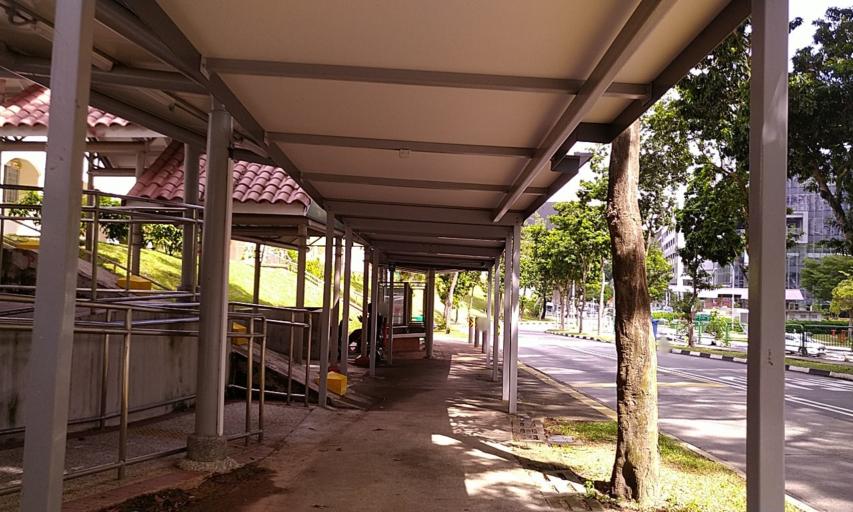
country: SG
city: Singapore
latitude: 1.2894
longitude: 103.8142
